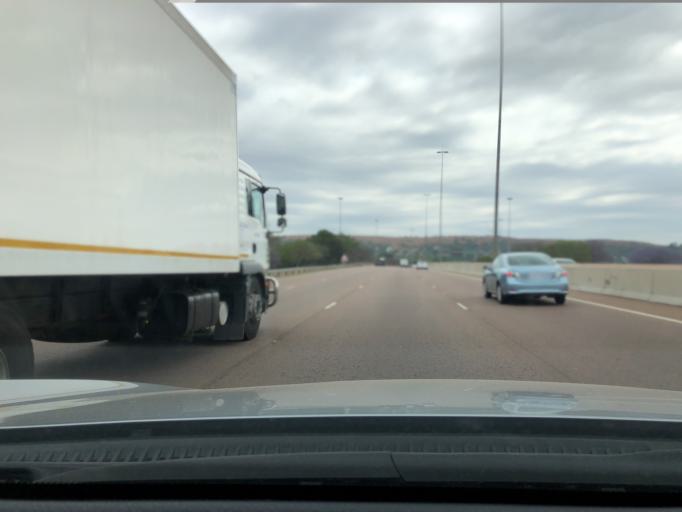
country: ZA
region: Gauteng
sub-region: City of Tshwane Metropolitan Municipality
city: Pretoria
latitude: -25.7138
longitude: 28.2655
